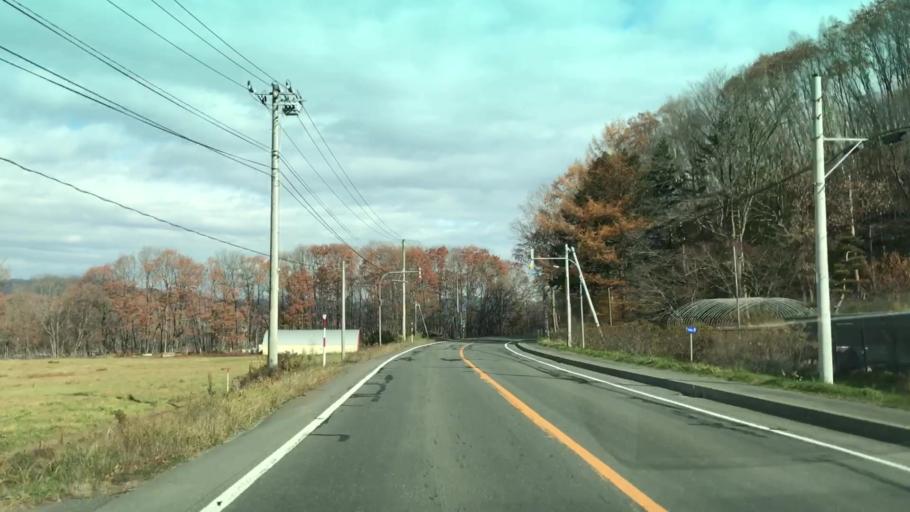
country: JP
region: Hokkaido
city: Shizunai-furukawacho
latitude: 42.6815
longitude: 142.2006
